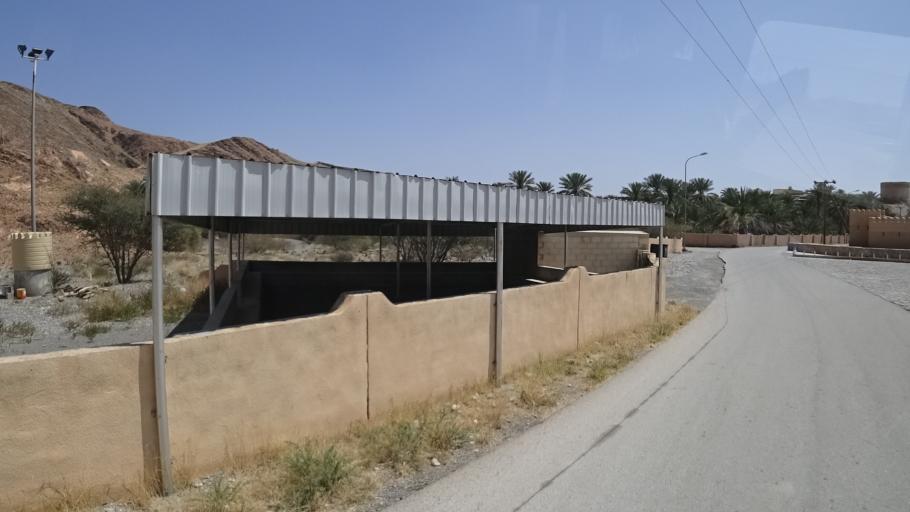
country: OM
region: Muhafazat ad Dakhiliyah
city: Izki
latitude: 22.9260
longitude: 57.6665
